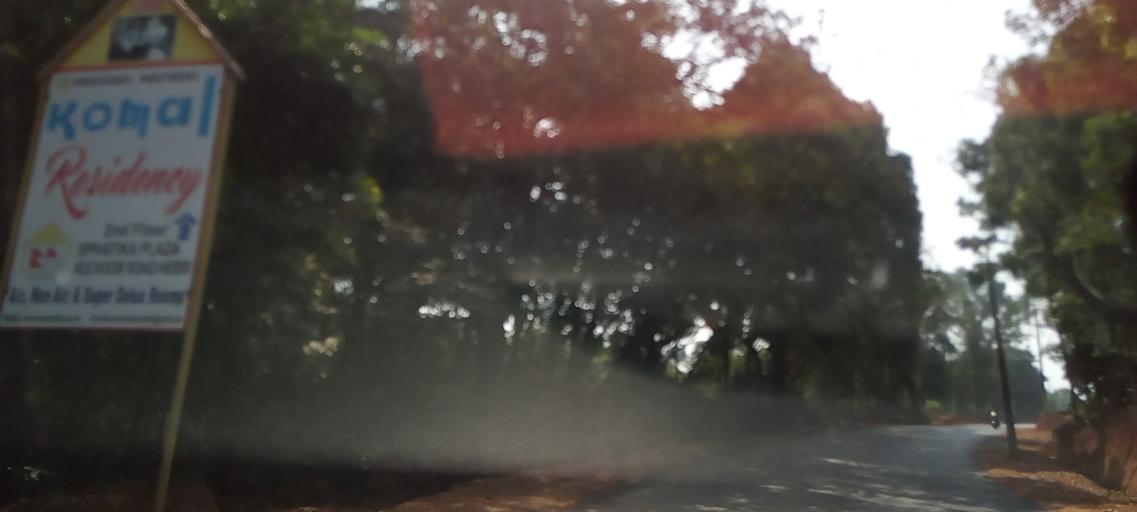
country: IN
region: Karnataka
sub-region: Udupi
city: Someshwar
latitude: 13.5259
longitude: 74.9269
